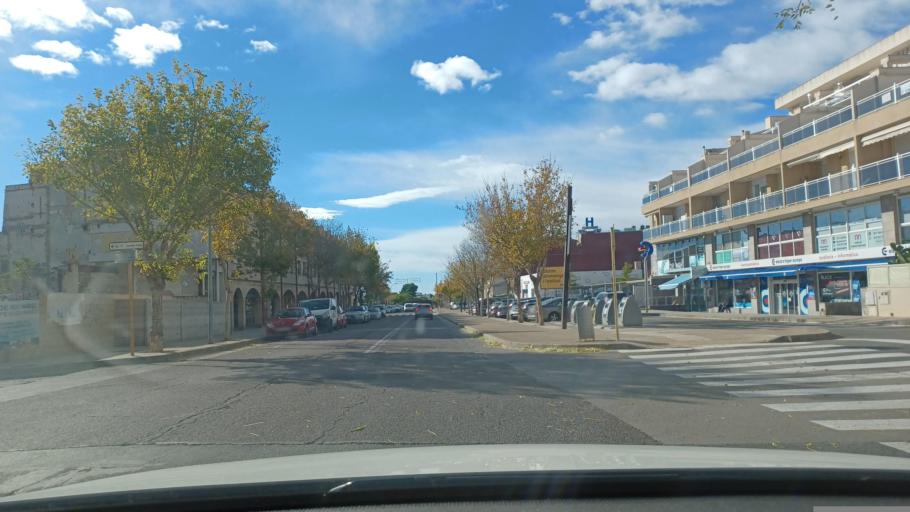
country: ES
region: Catalonia
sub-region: Provincia de Tarragona
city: Sant Carles de la Rapita
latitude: 40.6135
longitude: 0.5864
